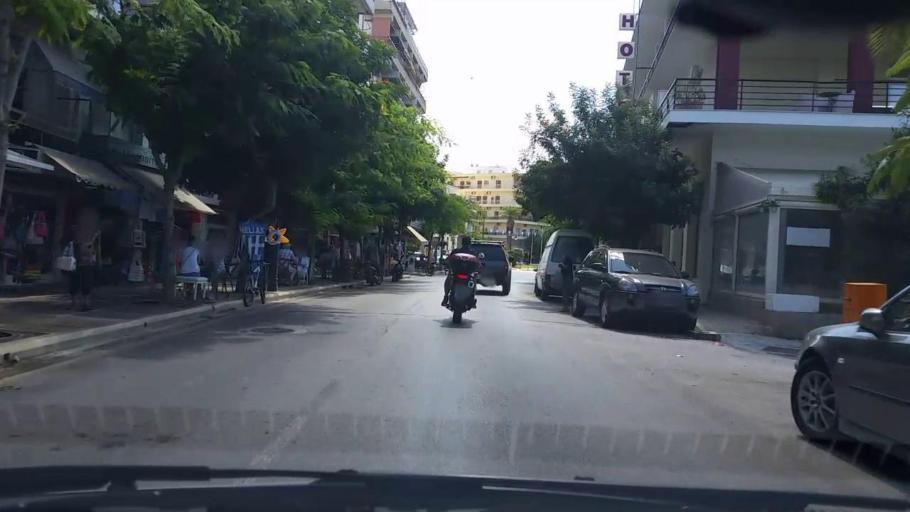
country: GR
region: Peloponnese
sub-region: Nomos Korinthias
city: Loutraki
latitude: 37.9792
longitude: 22.9766
